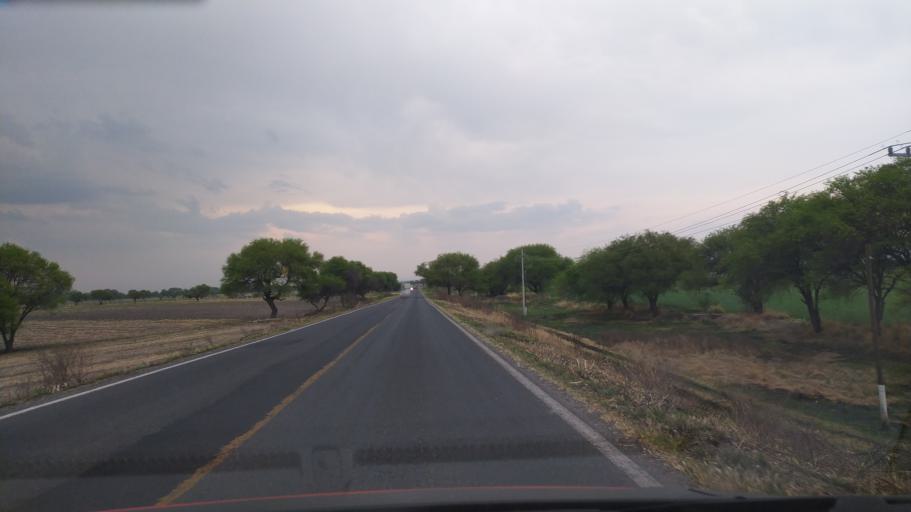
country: MX
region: Guanajuato
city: Ciudad Manuel Doblado
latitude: 20.7545
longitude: -101.9213
